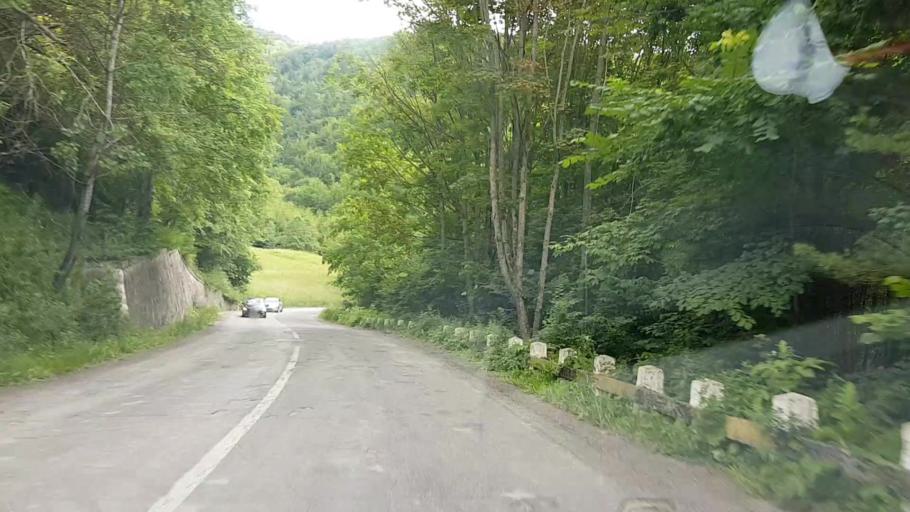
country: RO
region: Neamt
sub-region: Comuna Pangarati
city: Pangarati
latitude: 46.9363
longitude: 26.1265
